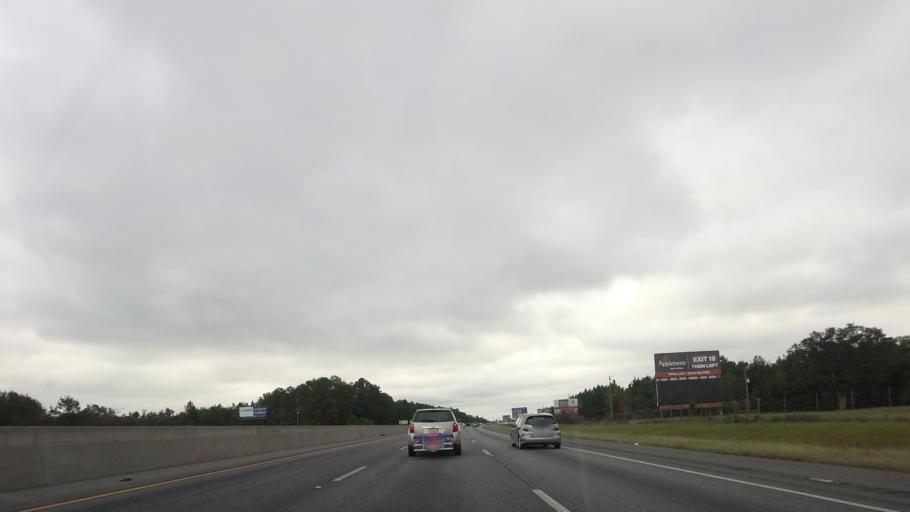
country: US
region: Georgia
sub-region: Lowndes County
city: Remerton
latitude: 30.8723
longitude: -83.3408
